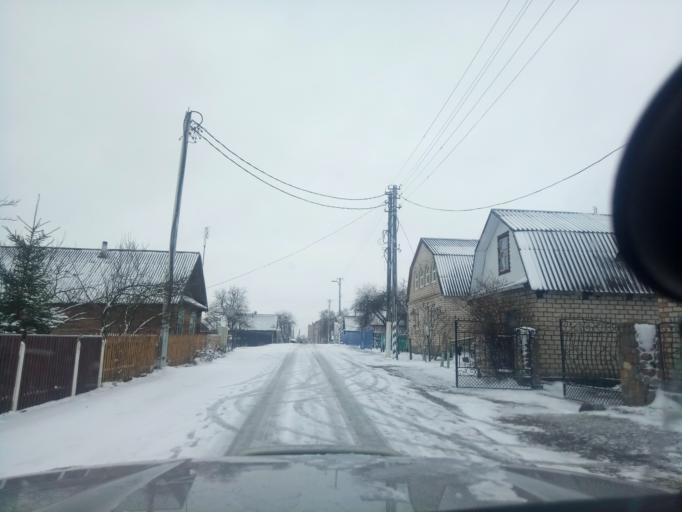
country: BY
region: Minsk
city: Kapyl'
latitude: 53.1535
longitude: 27.0824
